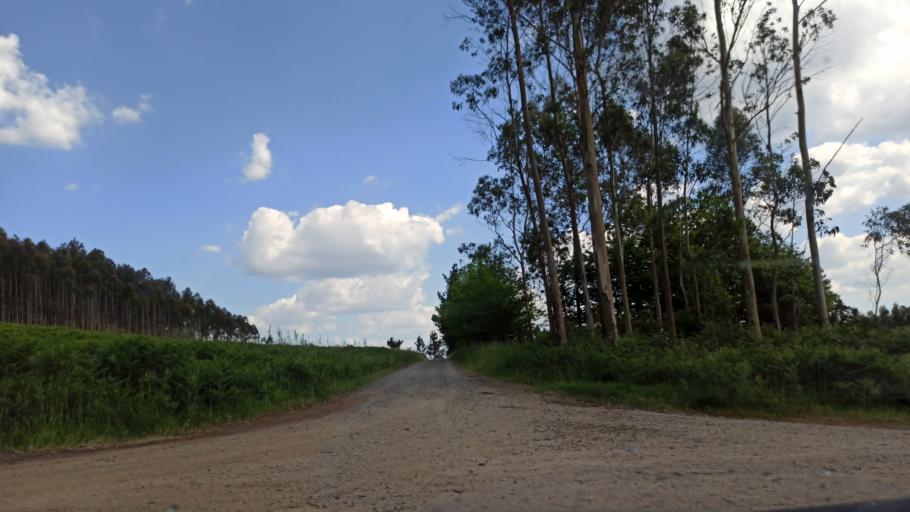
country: ES
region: Galicia
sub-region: Provincia da Coruna
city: Santa Comba
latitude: 43.0758
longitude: -8.7167
